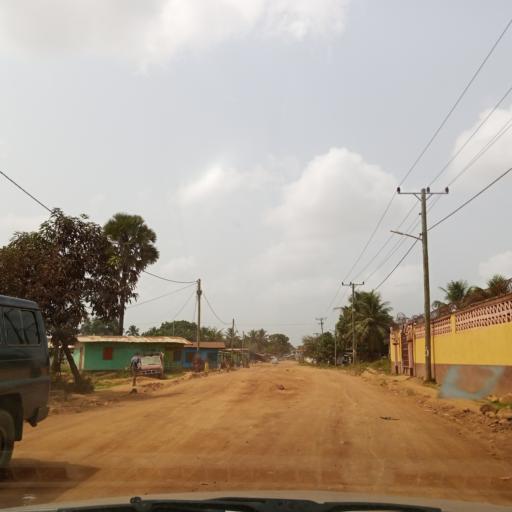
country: LR
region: Montserrado
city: Monrovia
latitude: 6.3498
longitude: -10.7290
